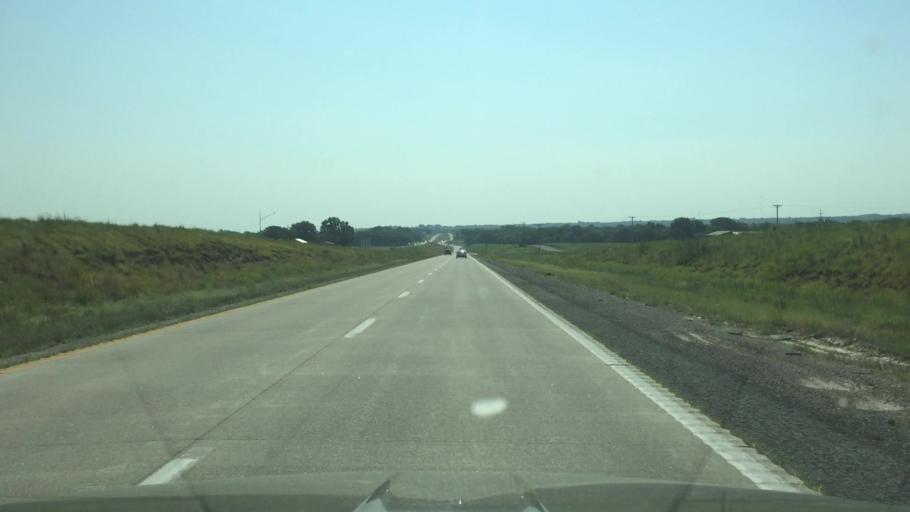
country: US
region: Missouri
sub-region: Johnson County
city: Warrensburg
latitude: 38.7729
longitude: -93.6844
